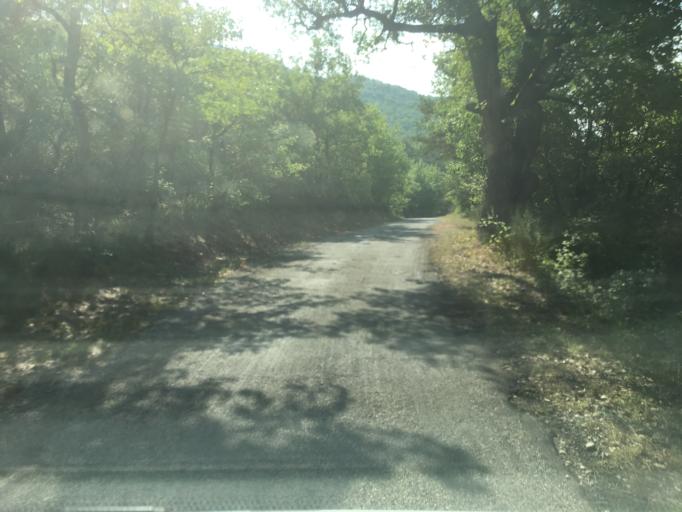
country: FR
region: Provence-Alpes-Cote d'Azur
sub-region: Departement des Alpes-de-Haute-Provence
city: Mallemoisson
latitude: 43.9280
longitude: 6.1902
